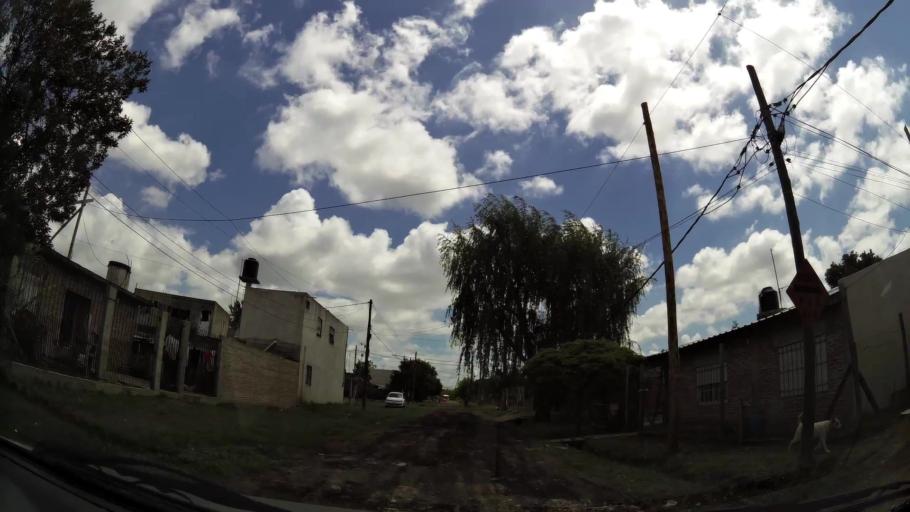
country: AR
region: Buenos Aires
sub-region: Partido de Quilmes
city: Quilmes
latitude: -34.8245
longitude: -58.2461
